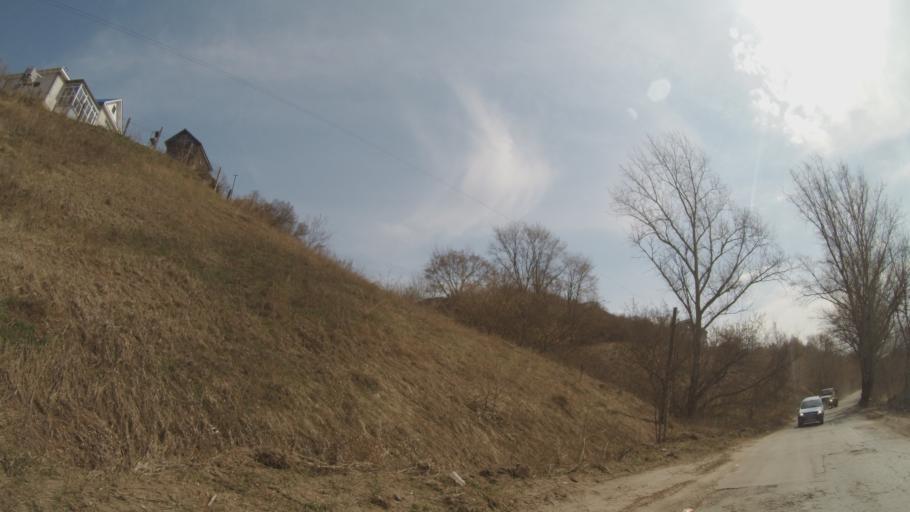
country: RU
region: Nizjnij Novgorod
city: Vyyezdnoye
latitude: 55.3914
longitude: 43.8079
